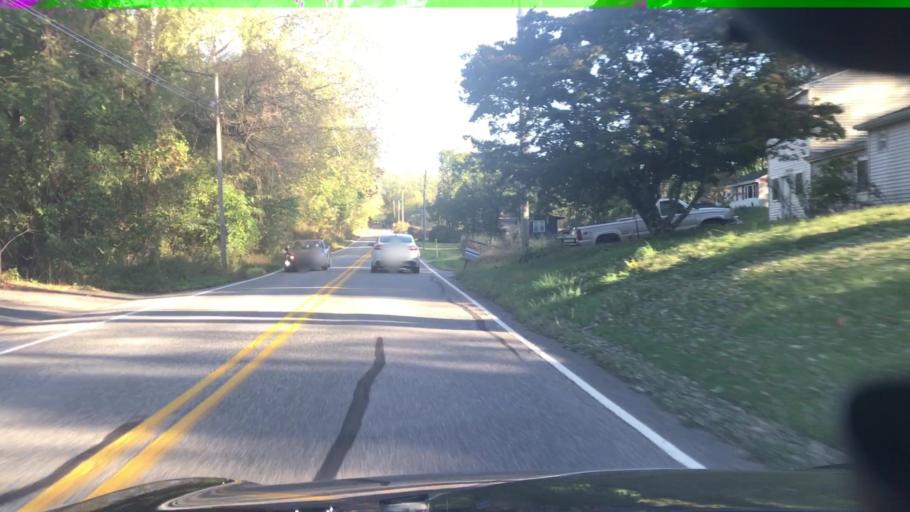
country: US
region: Pennsylvania
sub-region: Cumberland County
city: Lower Allen
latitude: 40.1670
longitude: -76.9010
